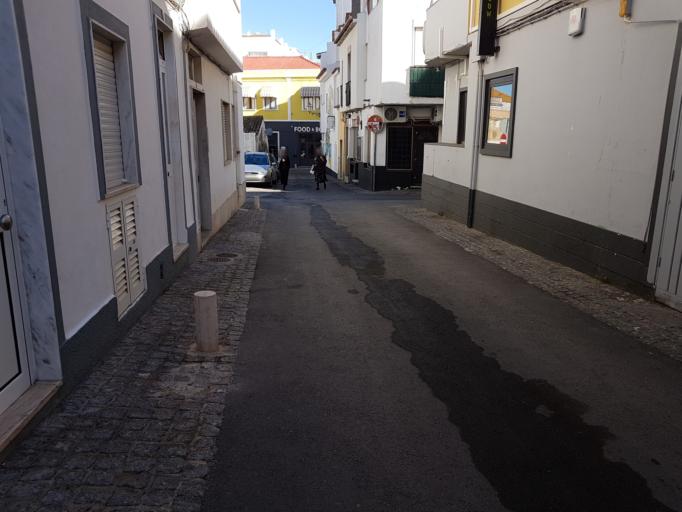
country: PT
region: Faro
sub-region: Lagos
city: Lagos
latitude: 37.1009
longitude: -8.6740
